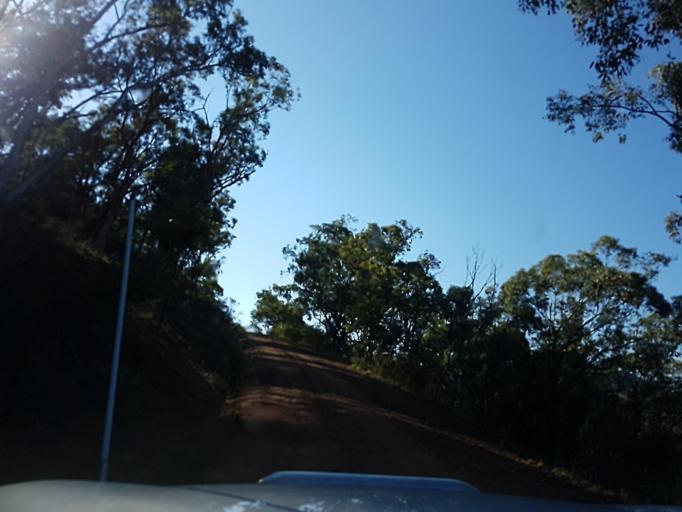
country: AU
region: New South Wales
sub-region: Snowy River
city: Jindabyne
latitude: -36.9319
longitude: 148.3351
